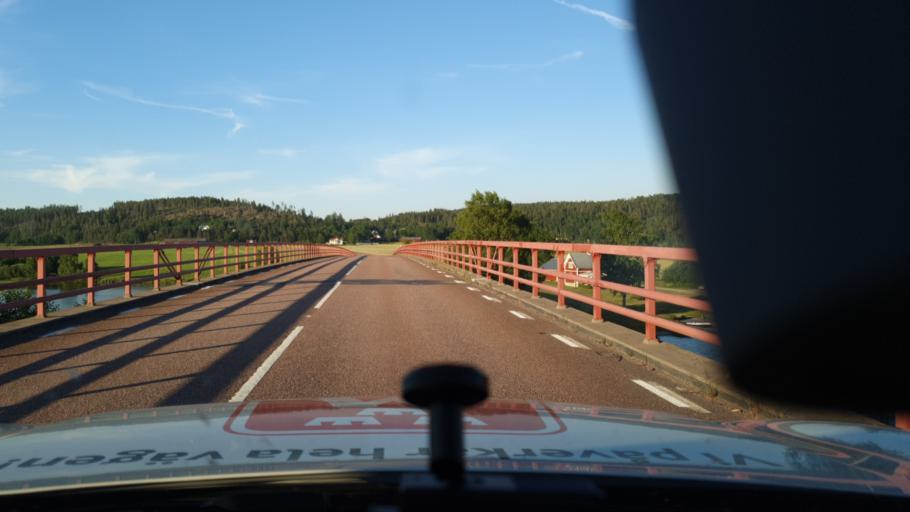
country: SE
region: Vaermland
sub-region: Kils Kommun
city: Kil
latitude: 59.6116
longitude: 13.3108
